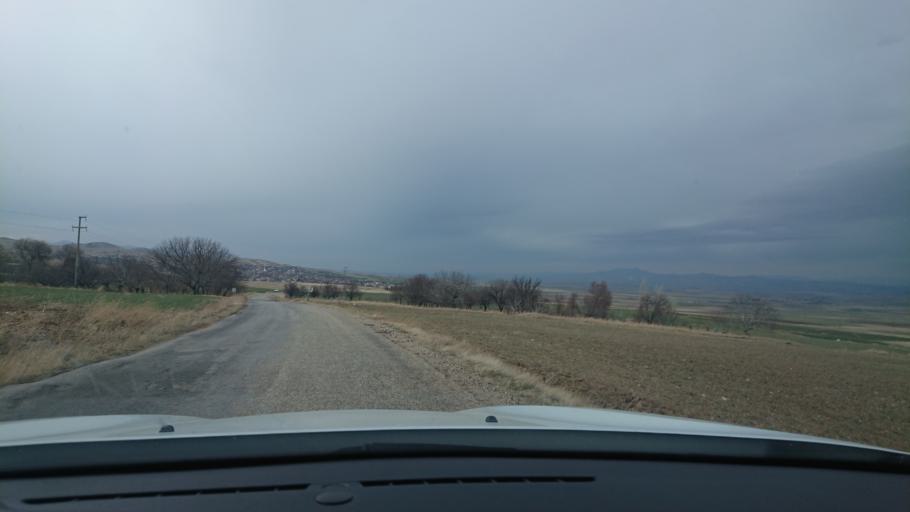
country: TR
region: Aksaray
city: Agacoren
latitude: 38.9464
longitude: 33.9072
